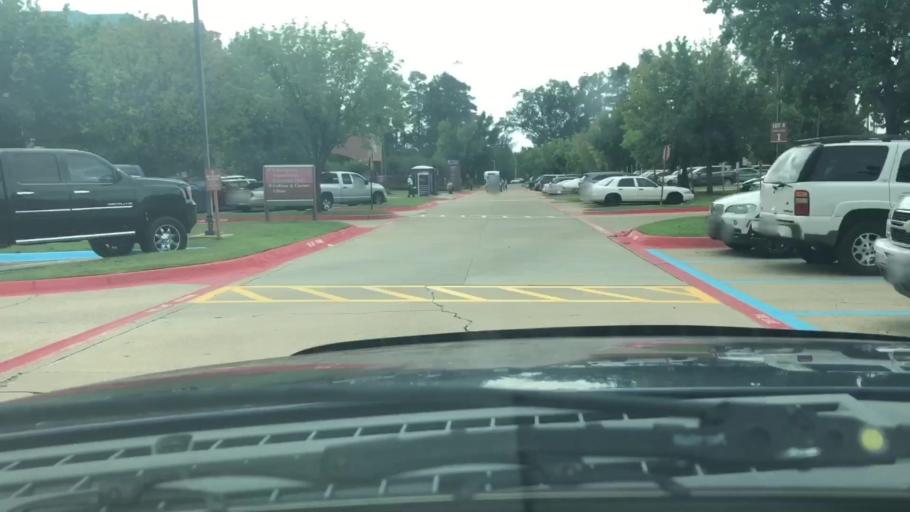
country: US
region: Arkansas
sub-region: Miller County
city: Texarkana
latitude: 33.4639
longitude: -94.0764
